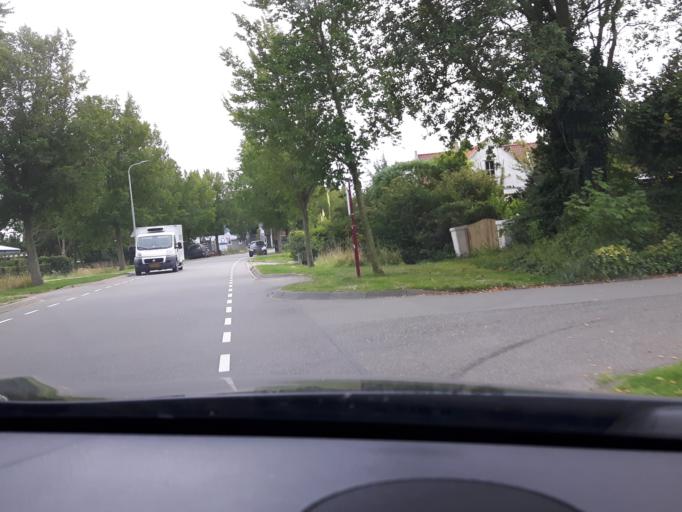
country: NL
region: Zeeland
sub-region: Schouwen-Duiveland
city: Scharendijke
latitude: 51.7321
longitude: 3.8417
